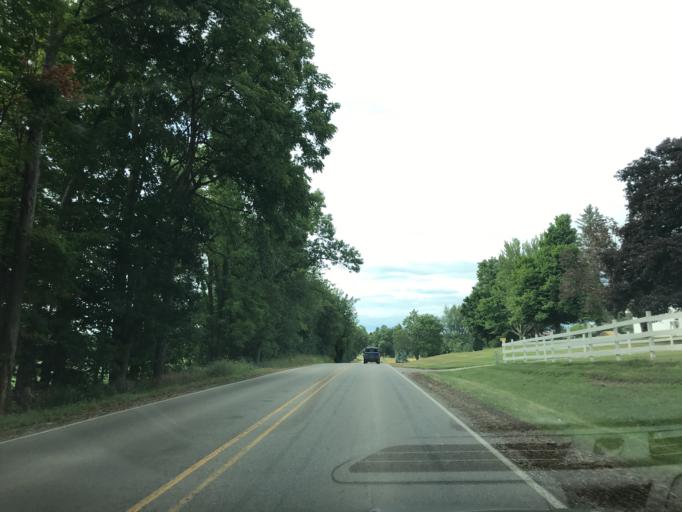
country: US
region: Michigan
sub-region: Jackson County
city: Spring Arbor
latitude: 42.0617
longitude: -84.5164
